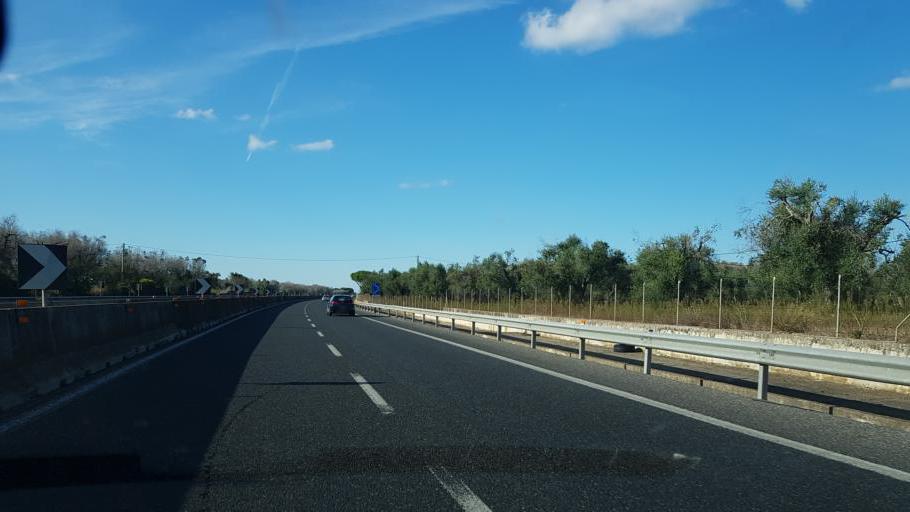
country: IT
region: Apulia
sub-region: Provincia di Brindisi
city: Torchiarolo
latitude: 40.4677
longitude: 18.0534
